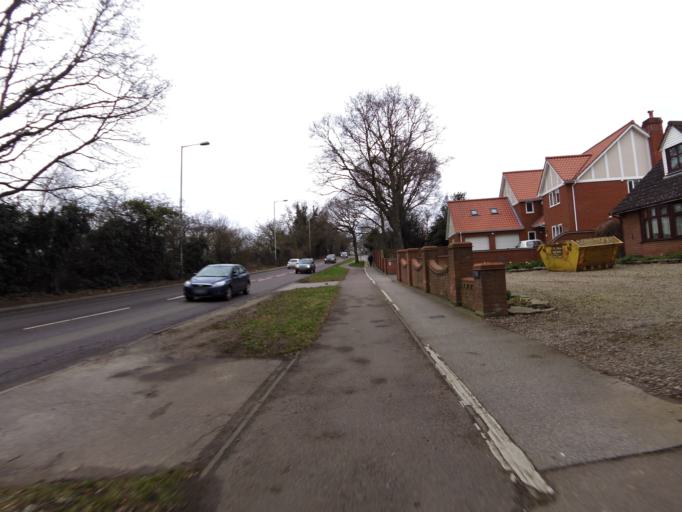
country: GB
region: England
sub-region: Norfolk
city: Hopton on Sea
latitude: 52.5047
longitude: 1.7326
